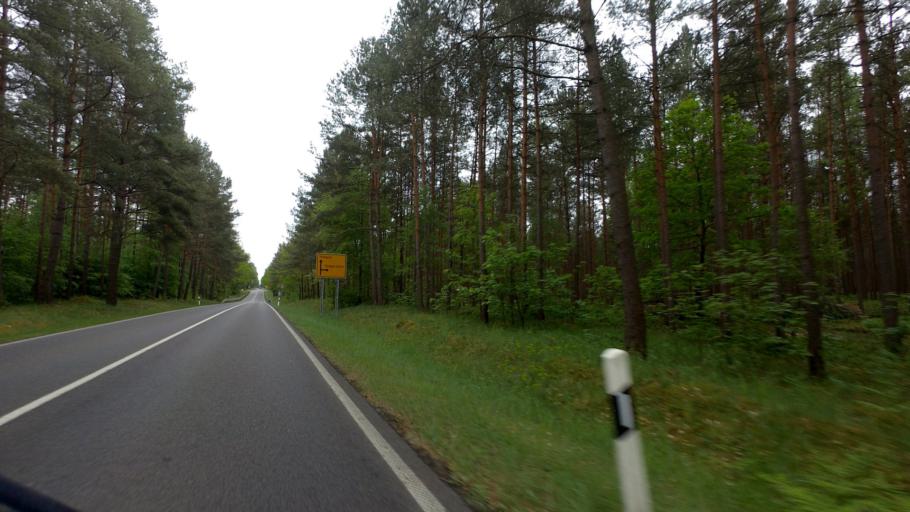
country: DE
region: Brandenburg
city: Lychen
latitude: 53.1698
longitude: 13.3383
